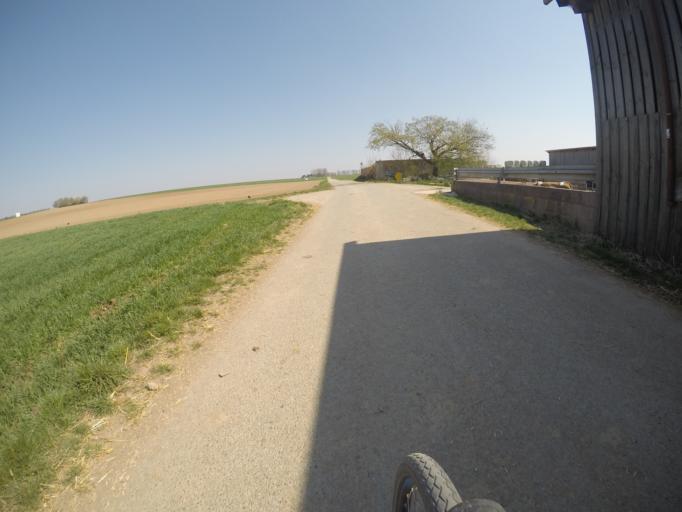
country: DE
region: Baden-Wuerttemberg
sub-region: Regierungsbezirk Stuttgart
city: Renningen
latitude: 48.7358
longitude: 8.9202
